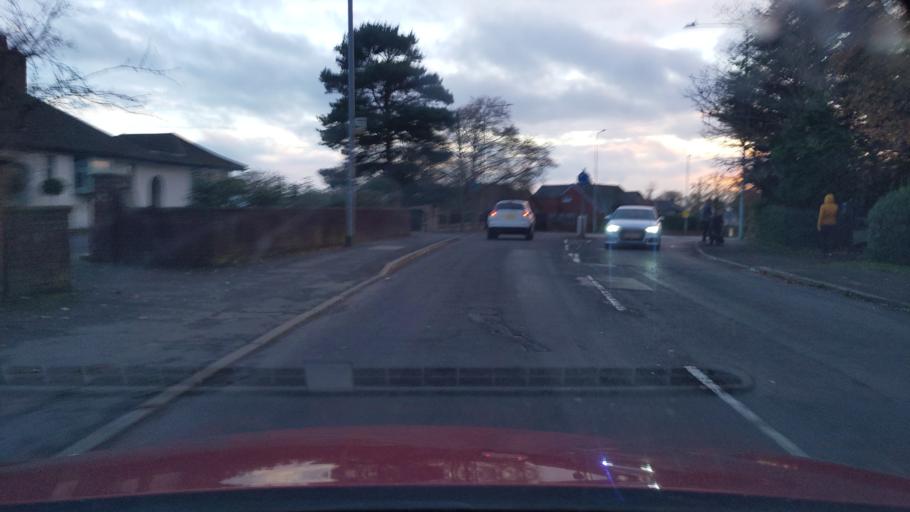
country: GB
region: England
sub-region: Lancashire
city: Clayton-le-Woods
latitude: 53.6984
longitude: -2.6606
